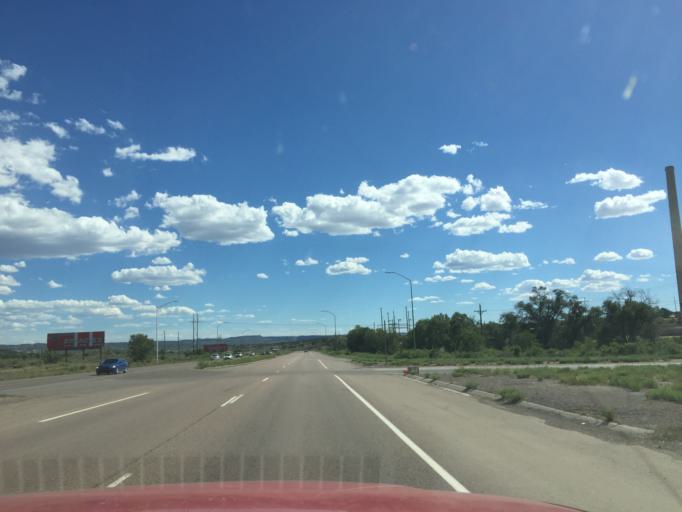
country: US
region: New Mexico
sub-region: McKinley County
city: Gallup
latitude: 35.5738
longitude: -108.7588
